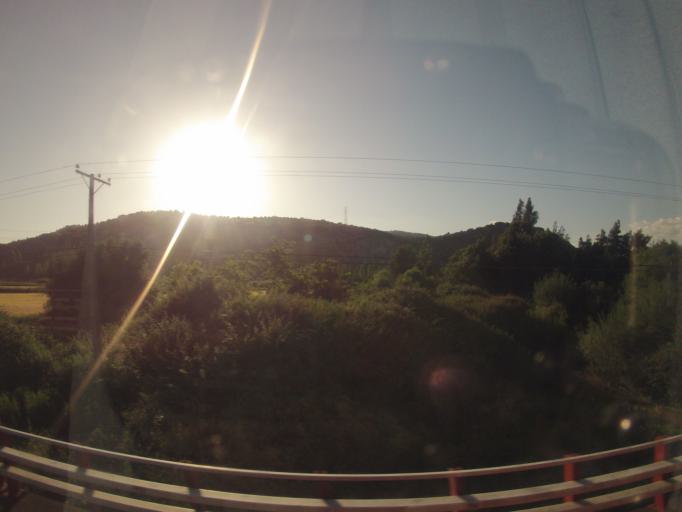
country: CL
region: O'Higgins
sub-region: Provincia de Colchagua
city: Chimbarongo
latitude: -34.6251
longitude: -70.9893
